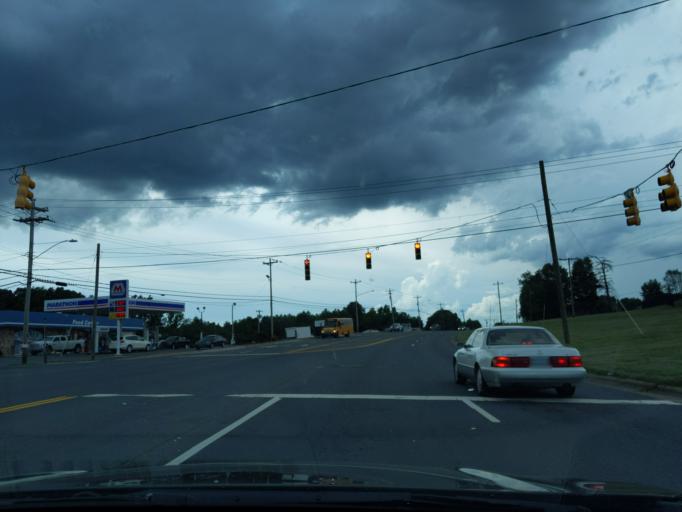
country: US
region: North Carolina
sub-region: Stanly County
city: Albemarle
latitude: 35.3980
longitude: -80.2008
